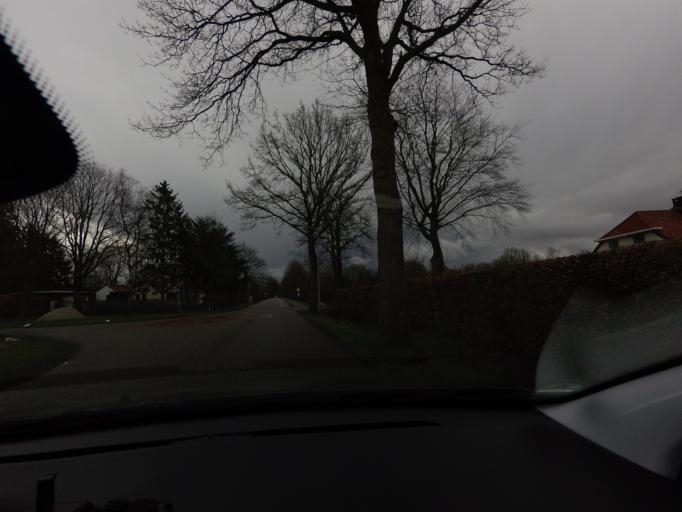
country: NL
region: Drenthe
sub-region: Gemeente Borger-Odoorn
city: Borger
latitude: 52.9898
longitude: 6.7770
